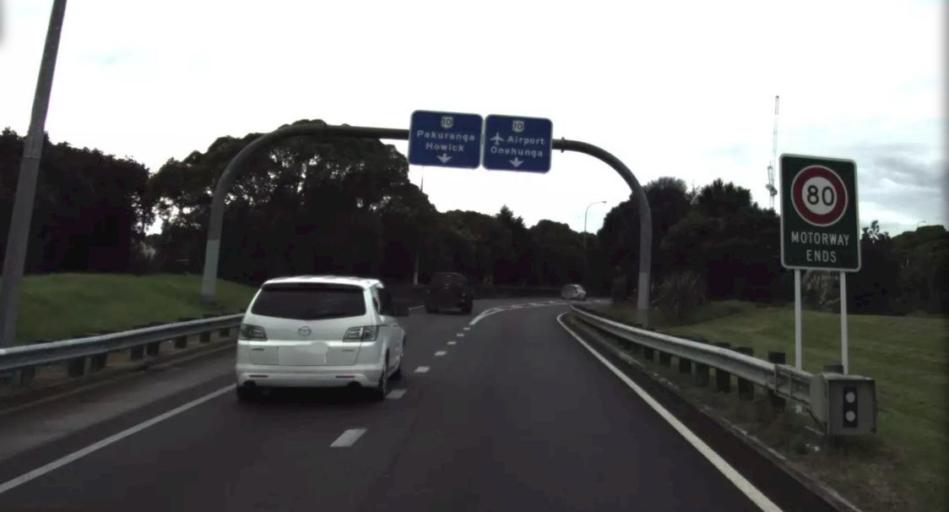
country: NZ
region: Auckland
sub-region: Auckland
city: Tamaki
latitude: -36.9160
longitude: 174.8346
